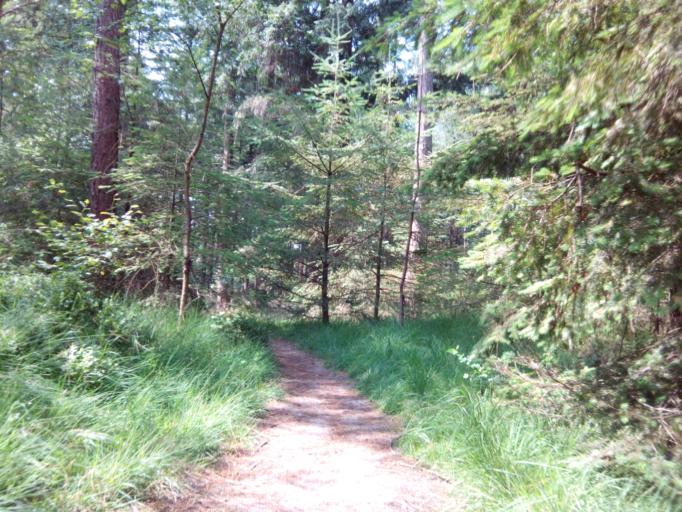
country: NL
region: Utrecht
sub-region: Gemeente Utrechtse Heuvelrug
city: Maarn
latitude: 52.0938
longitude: 5.3761
